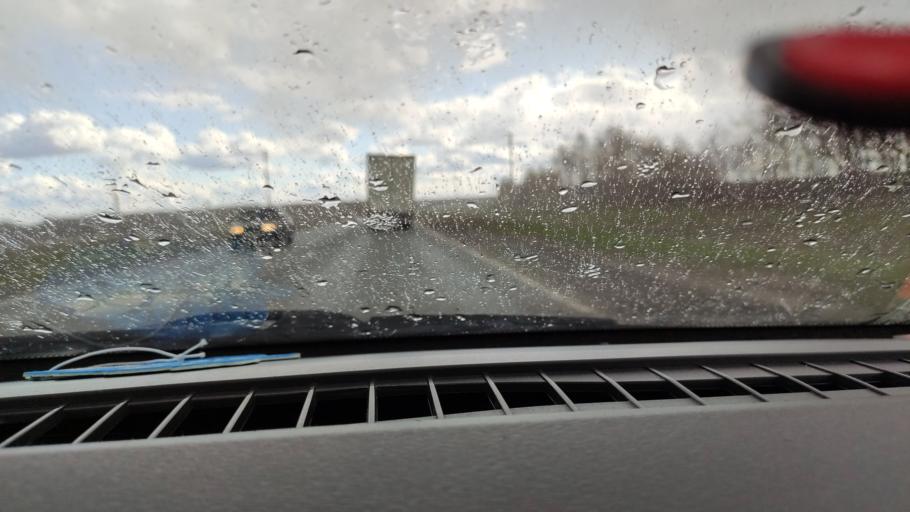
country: RU
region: Saratov
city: Balakovo
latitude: 52.1121
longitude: 47.7494
